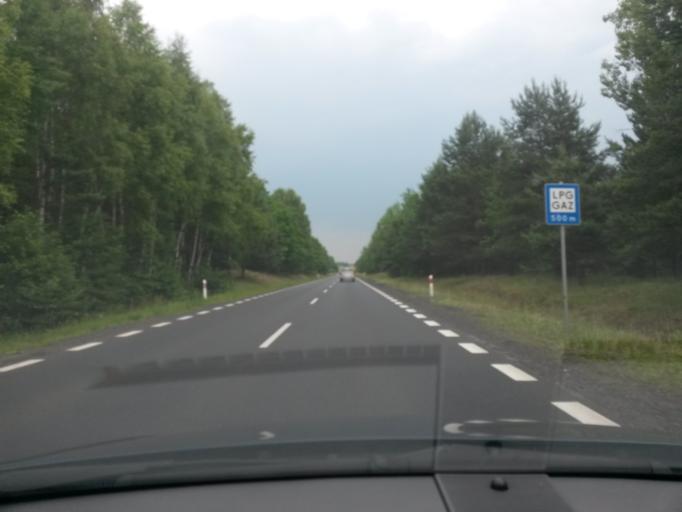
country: PL
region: Silesian Voivodeship
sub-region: Powiat czestochowski
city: Olsztyn
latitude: 50.7601
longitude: 19.2178
